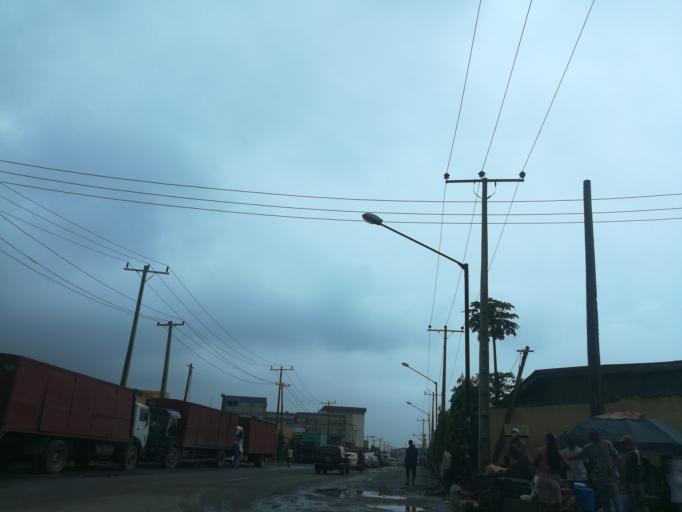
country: NG
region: Lagos
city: Agege
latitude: 6.6137
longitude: 3.3320
